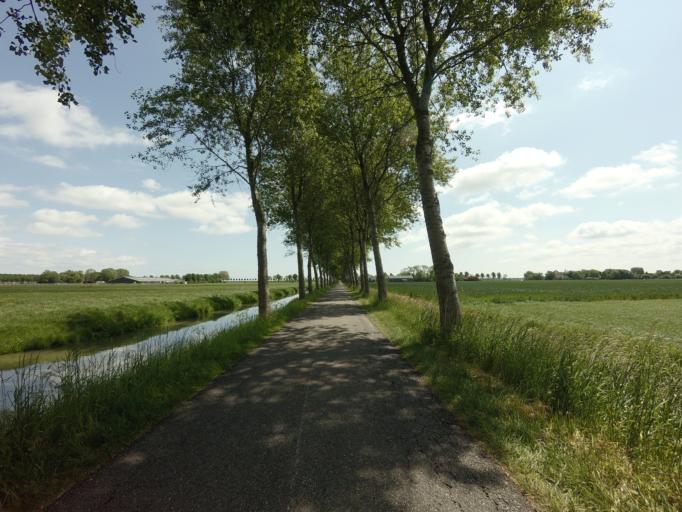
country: NL
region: North Holland
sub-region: Gemeente Beemster
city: Halfweg
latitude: 52.5970
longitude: 4.9355
